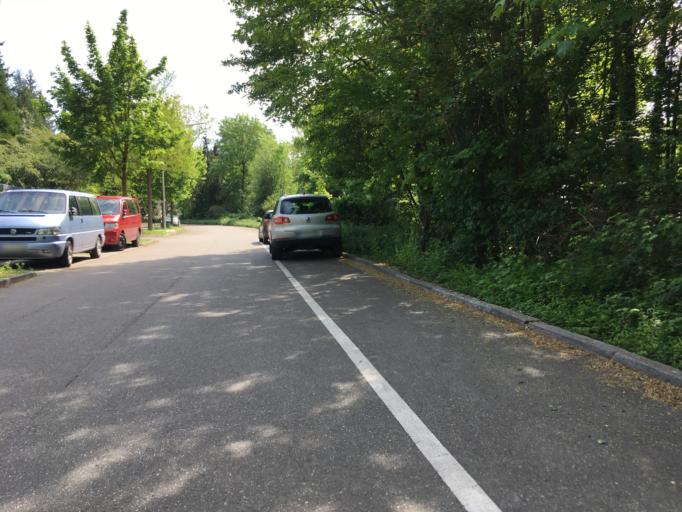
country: DE
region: Baden-Wuerttemberg
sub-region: Regierungsbezirk Stuttgart
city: Heilbronn
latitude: 49.1379
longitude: 9.2399
